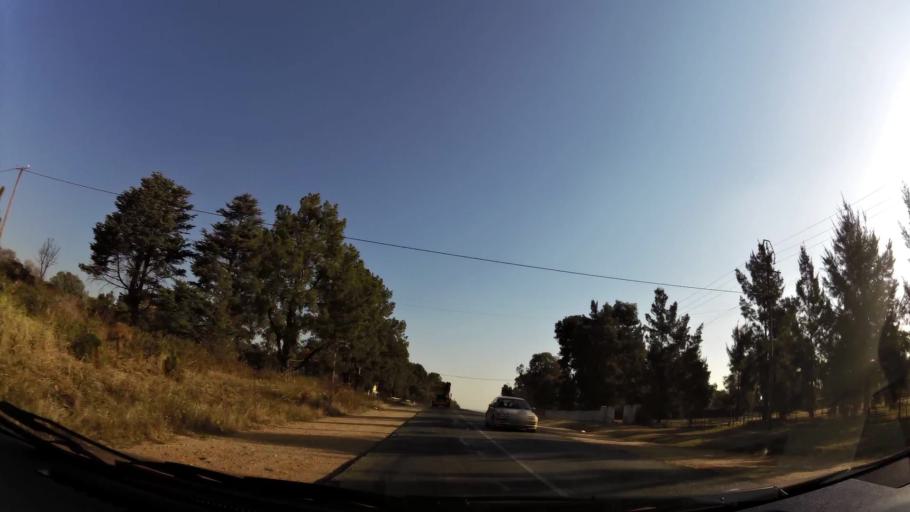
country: ZA
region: Gauteng
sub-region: West Rand District Municipality
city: Muldersdriseloop
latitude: -26.0181
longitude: 27.8832
